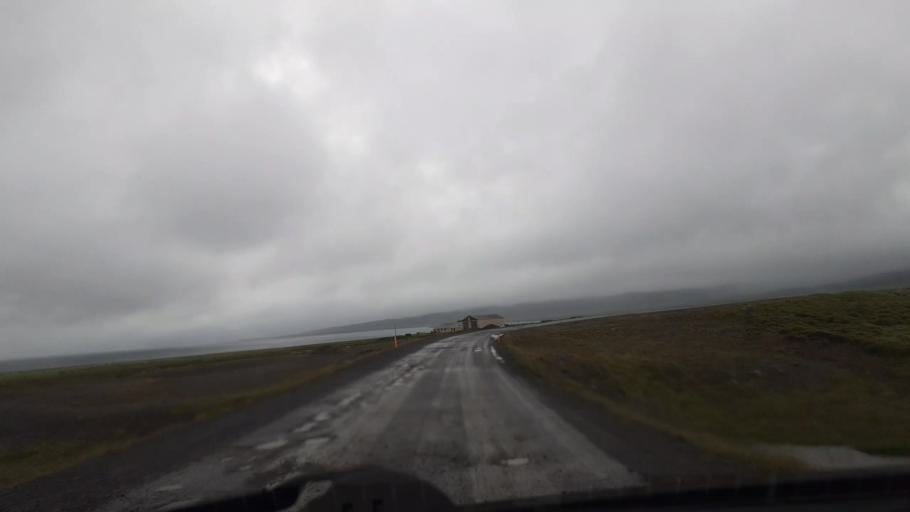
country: IS
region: East
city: Egilsstadir
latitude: 66.0694
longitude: -15.0889
